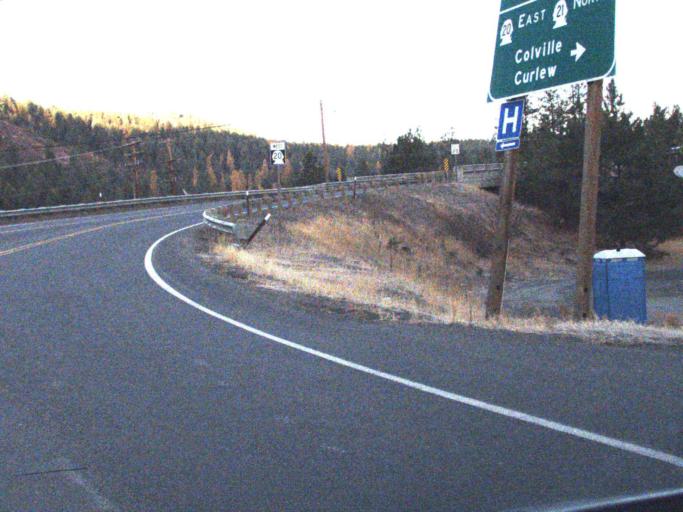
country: US
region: Washington
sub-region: Ferry County
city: Republic
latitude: 48.6404
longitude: -118.7339
